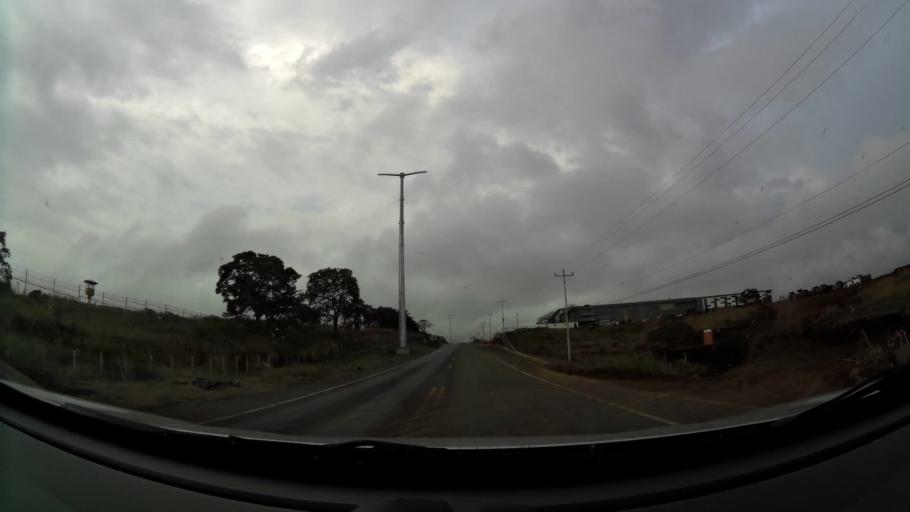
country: CR
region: Alajuela
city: Carrillos
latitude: 9.9737
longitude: -84.2778
